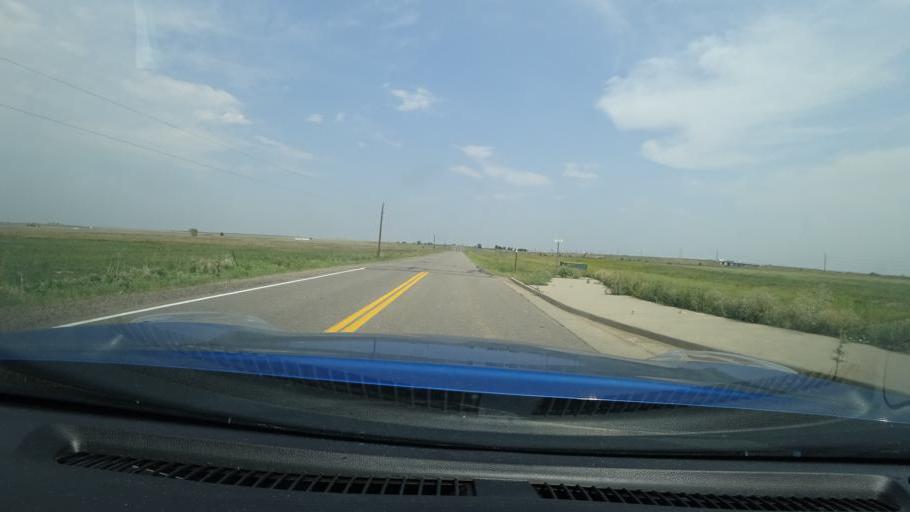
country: US
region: Colorado
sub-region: Adams County
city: Aurora
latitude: 39.7547
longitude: -104.7262
